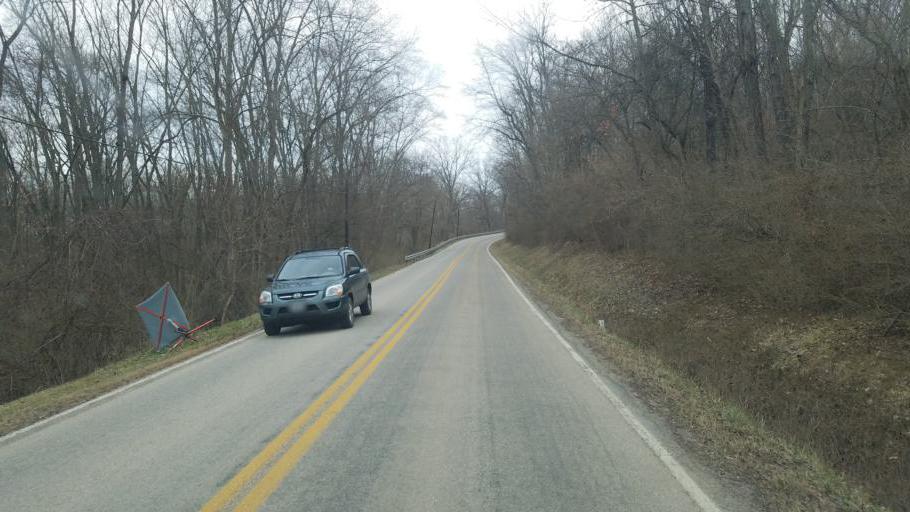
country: US
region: Ohio
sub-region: Ashland County
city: Loudonville
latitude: 40.6477
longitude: -82.2430
